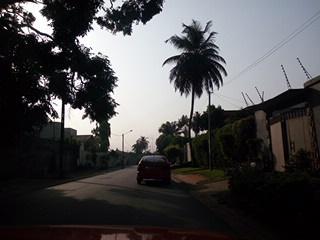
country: CI
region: Lagunes
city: Abobo
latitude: 5.3770
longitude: -3.9898
